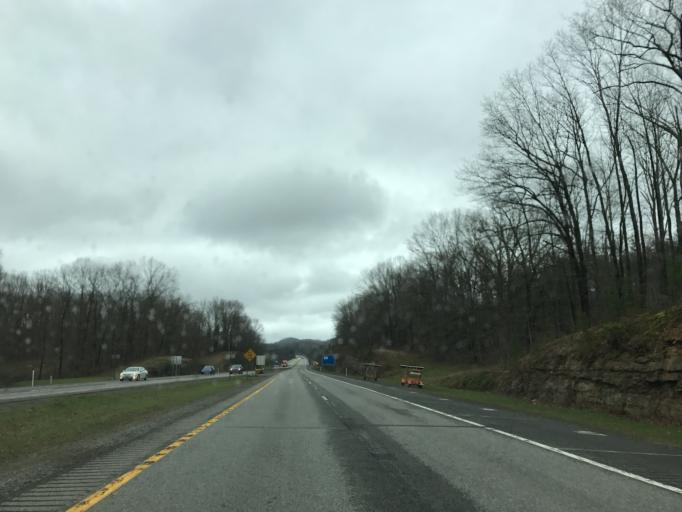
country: US
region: West Virginia
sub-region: Fayette County
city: Fayetteville
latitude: 38.0640
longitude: -81.0920
